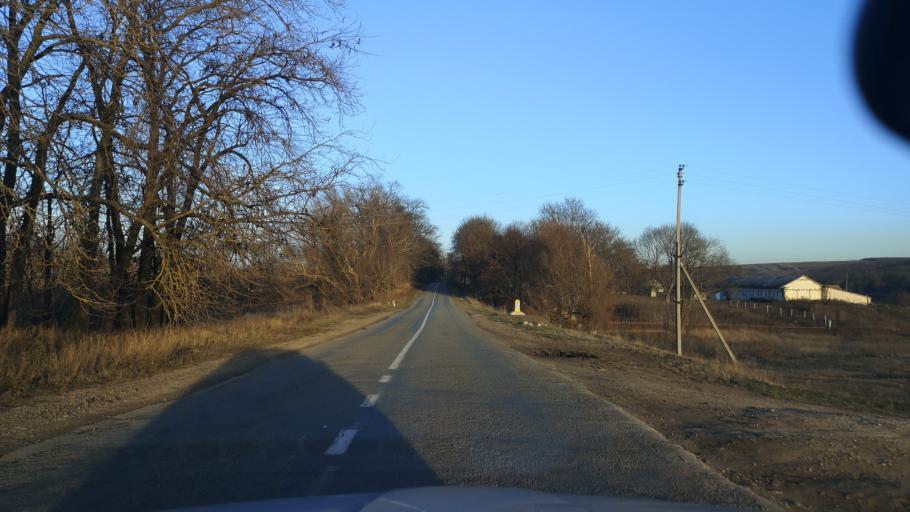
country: MD
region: Orhei
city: Orhei
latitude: 47.2922
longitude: 28.8914
